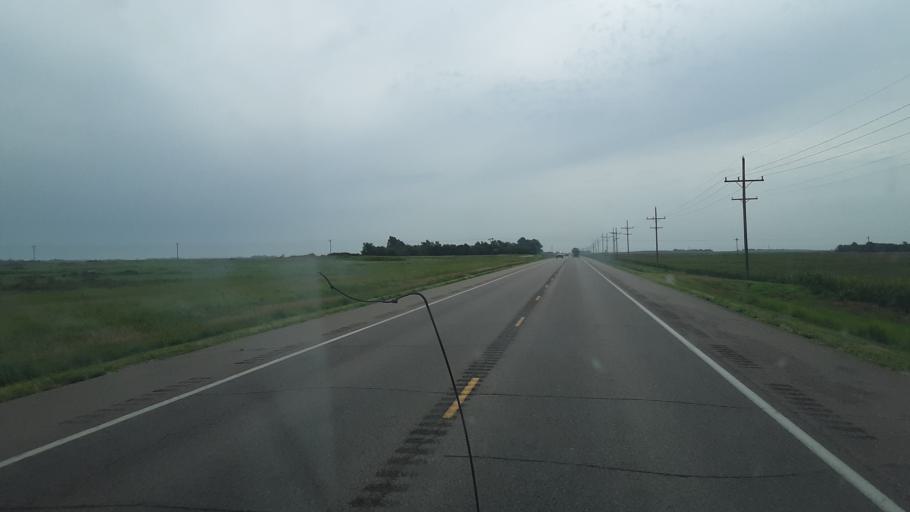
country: US
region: Kansas
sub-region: Edwards County
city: Kinsley
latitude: 37.9274
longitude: -99.3183
